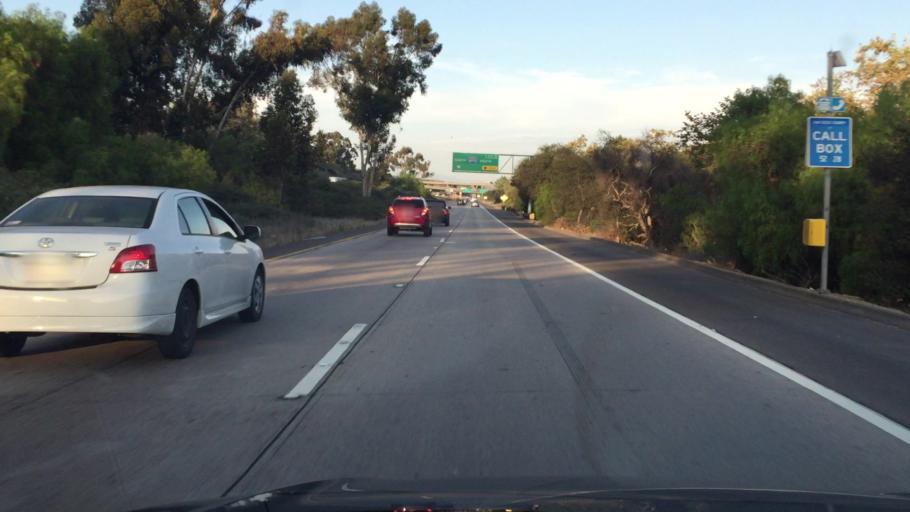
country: US
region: California
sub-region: San Diego County
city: La Jolla
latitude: 32.8456
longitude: -117.1926
